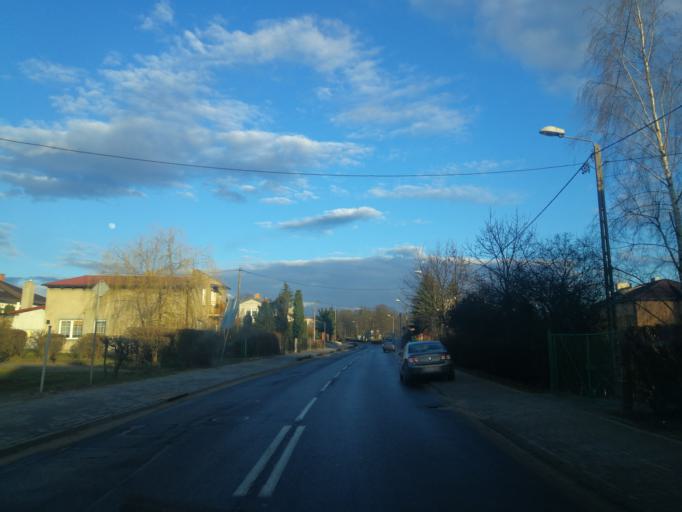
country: PL
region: Kujawsko-Pomorskie
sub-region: Powiat torunski
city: Chelmza
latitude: 53.1898
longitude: 18.6158
